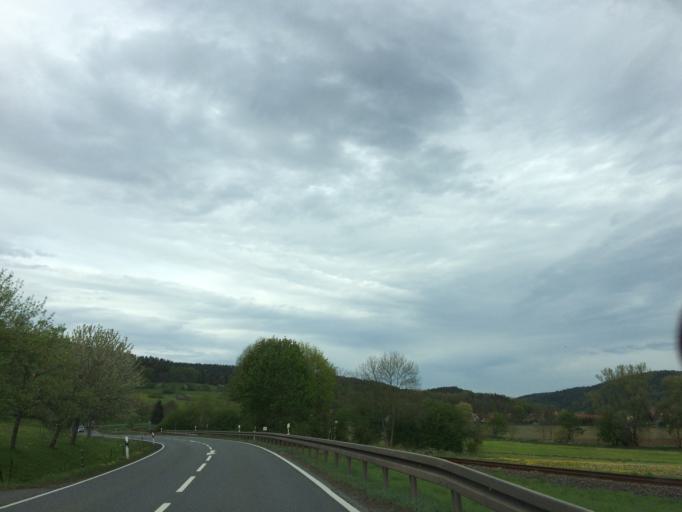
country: DE
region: Thuringia
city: Langenorla
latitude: 50.7279
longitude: 11.6001
